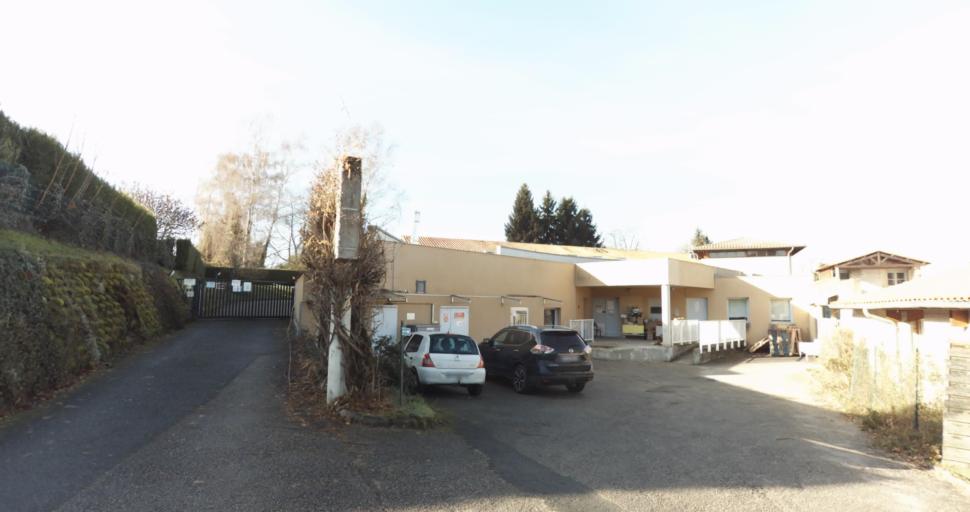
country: FR
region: Limousin
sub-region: Departement de la Haute-Vienne
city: Aixe-sur-Vienne
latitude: 45.7944
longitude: 1.1291
